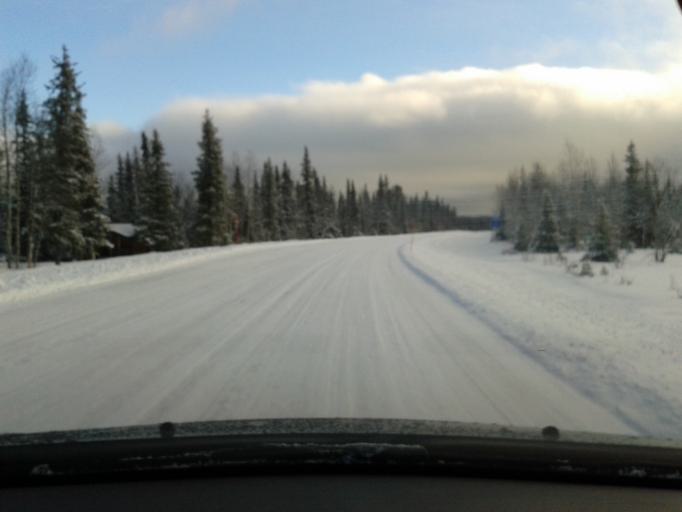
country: SE
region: Vaesterbotten
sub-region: Vilhelmina Kommun
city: Sjoberg
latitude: 65.2582
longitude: 15.6818
